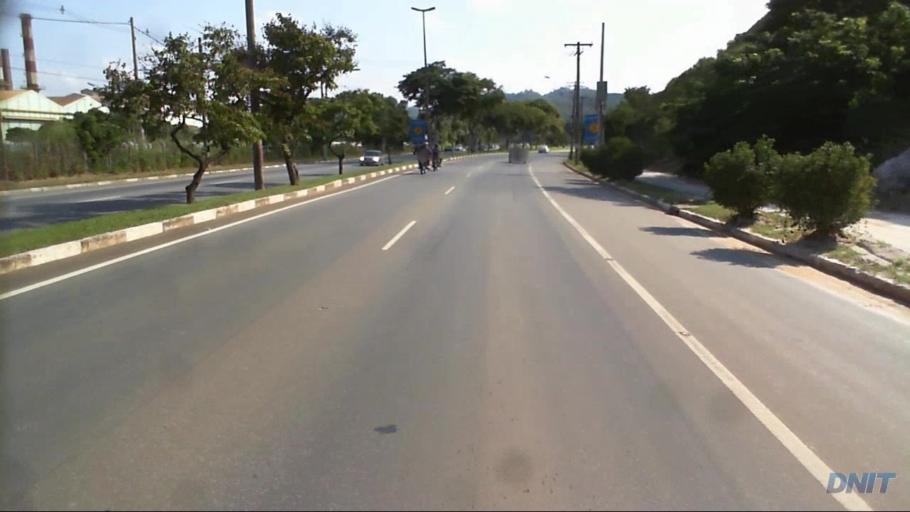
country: BR
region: Minas Gerais
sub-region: Ipatinga
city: Ipatinga
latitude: -19.4828
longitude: -42.5486
